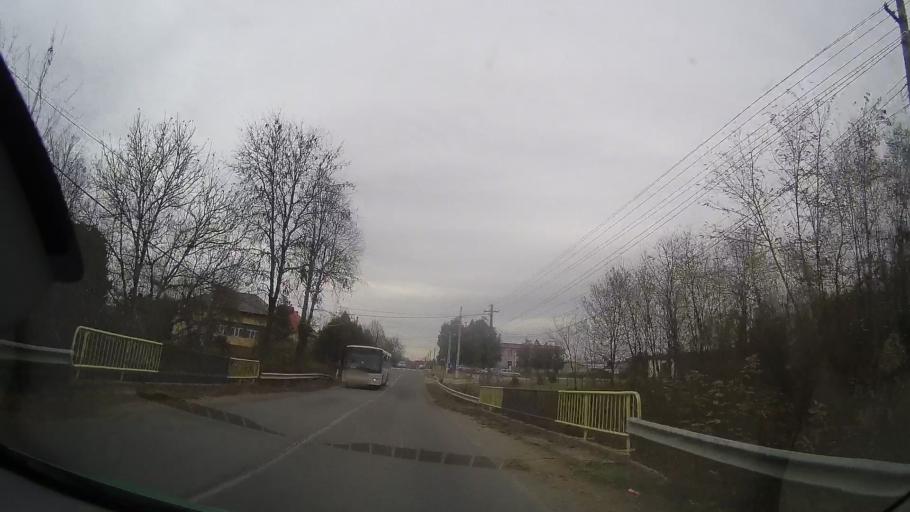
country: RO
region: Prahova
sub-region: Comuna Iordachianu
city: Iordacheanu
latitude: 45.0429
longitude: 26.2378
